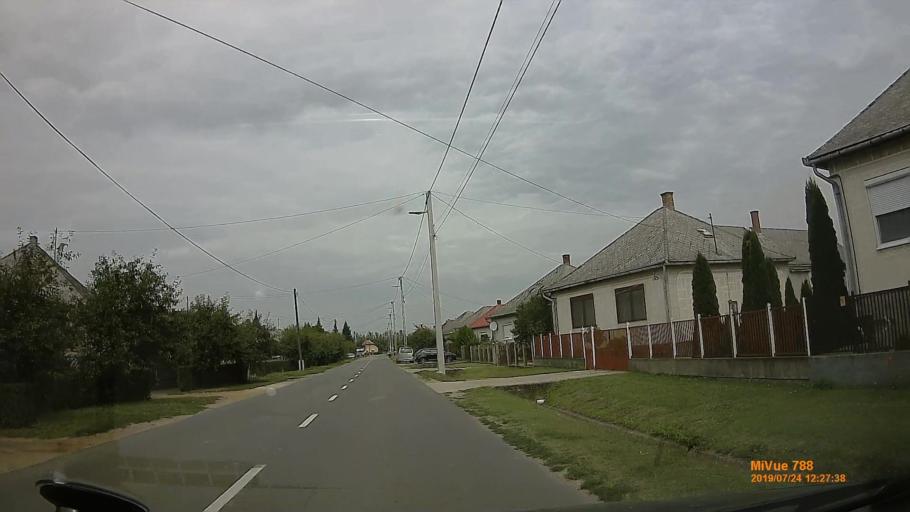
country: HU
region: Szabolcs-Szatmar-Bereg
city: Vasarosnameny
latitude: 48.1376
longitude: 22.3430
